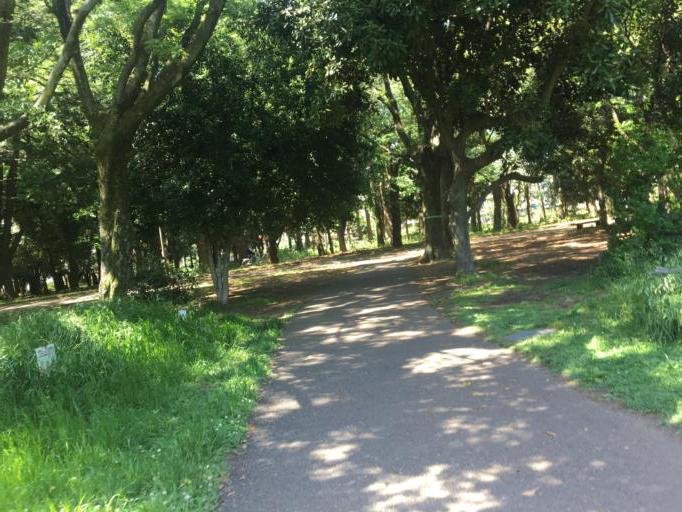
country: JP
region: Saitama
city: Wako
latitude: 35.7691
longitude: 139.6342
